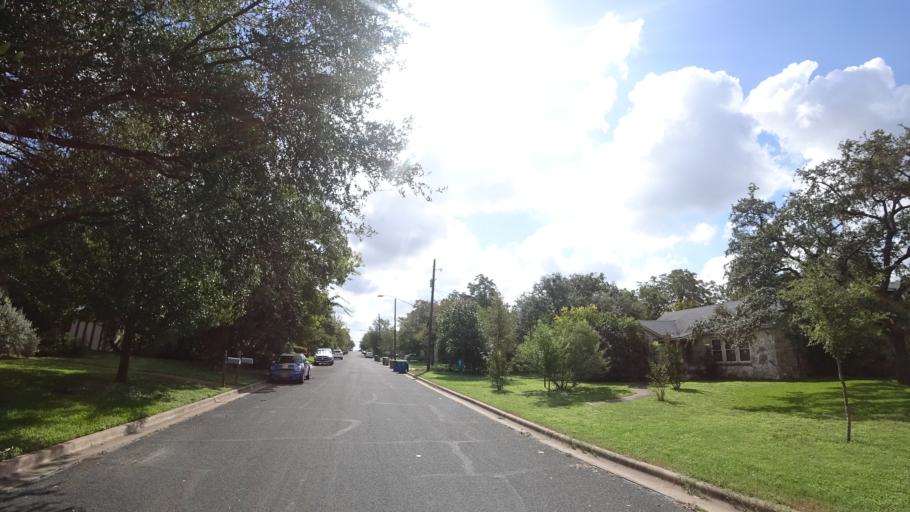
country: US
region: Texas
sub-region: Travis County
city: Austin
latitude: 30.3478
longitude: -97.7200
